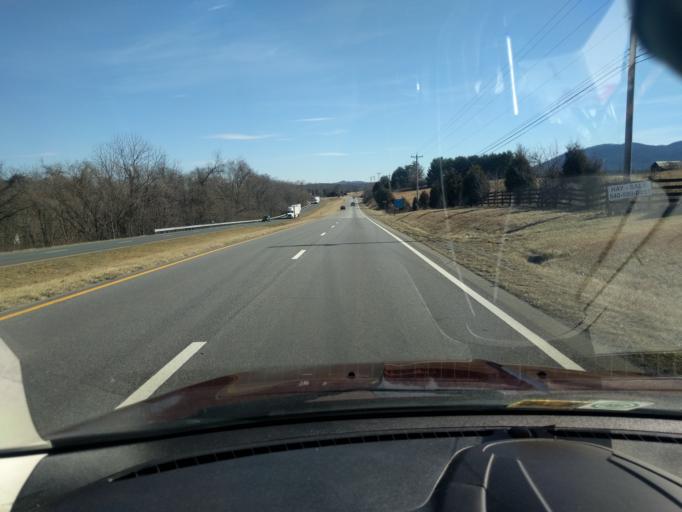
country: US
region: Virginia
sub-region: Botetourt County
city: Blue Ridge
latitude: 37.3592
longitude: -79.6754
